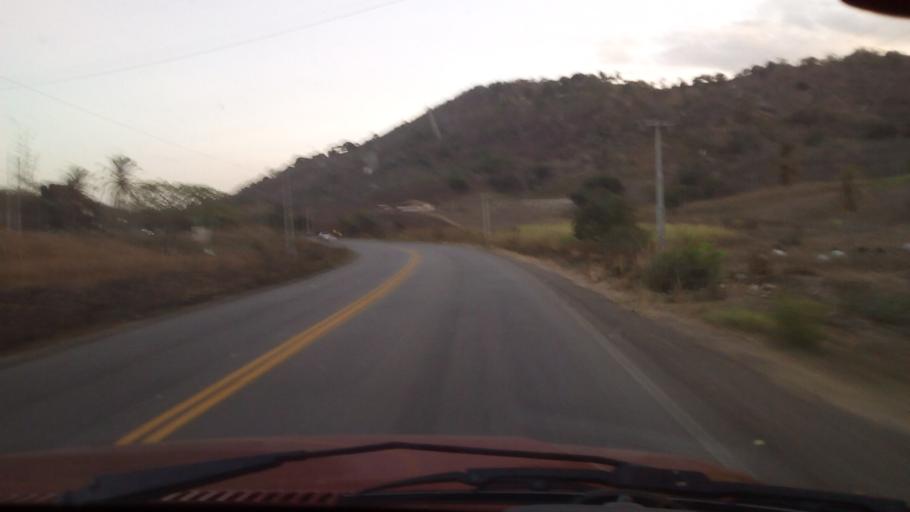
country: BR
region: Paraiba
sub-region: Bananeiras
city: Solanea
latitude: -6.7353
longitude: -35.5376
